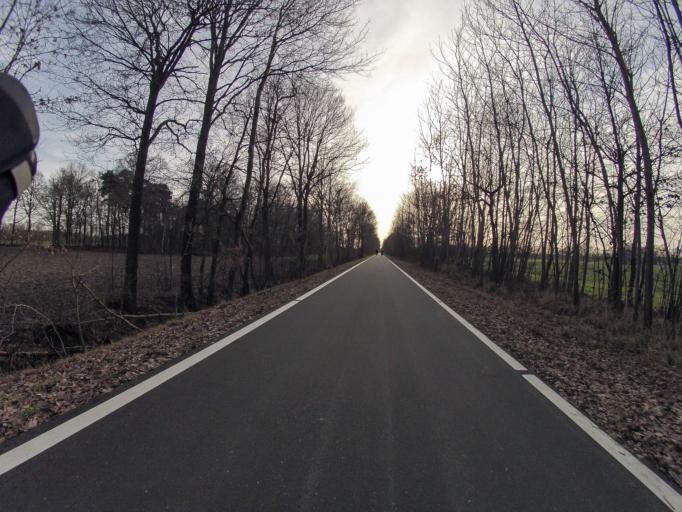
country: DE
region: North Rhine-Westphalia
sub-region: Regierungsbezirk Munster
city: Steinfurt
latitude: 52.1840
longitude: 7.3707
